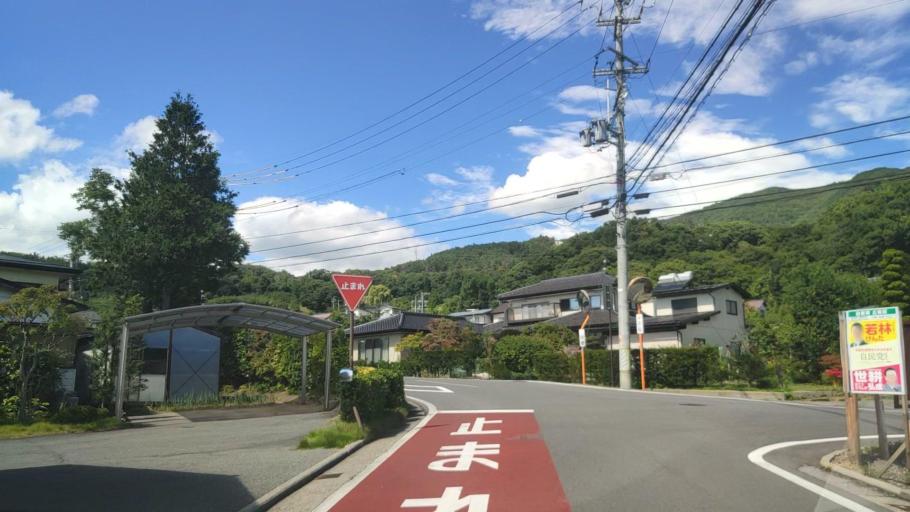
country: JP
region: Nagano
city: Nagano-shi
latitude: 36.6881
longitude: 138.2171
